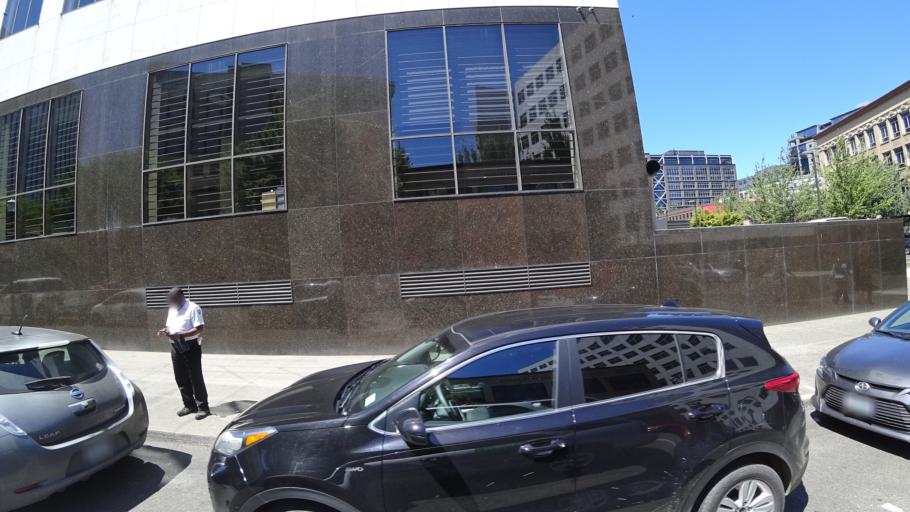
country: US
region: Oregon
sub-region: Multnomah County
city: Portland
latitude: 45.5223
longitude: -122.6801
